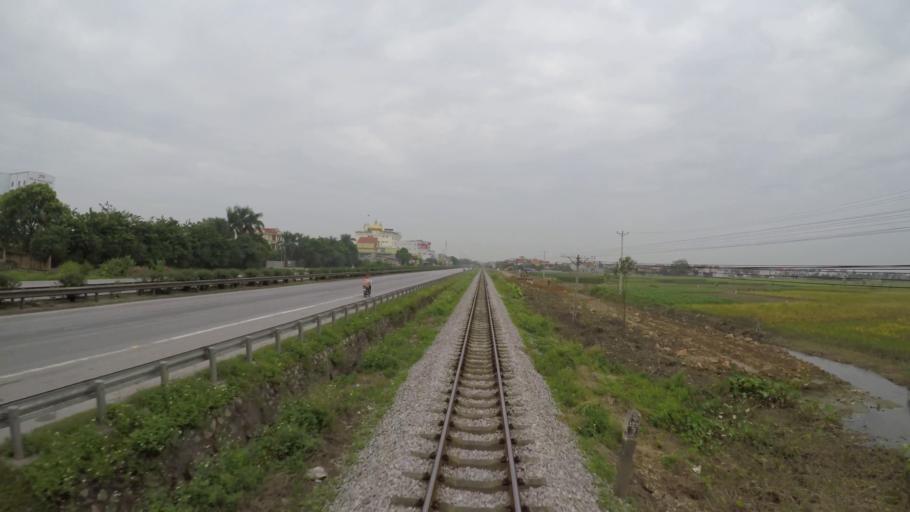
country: VN
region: Hai Duong
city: Thanh Ha
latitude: 20.9780
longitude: 106.4162
